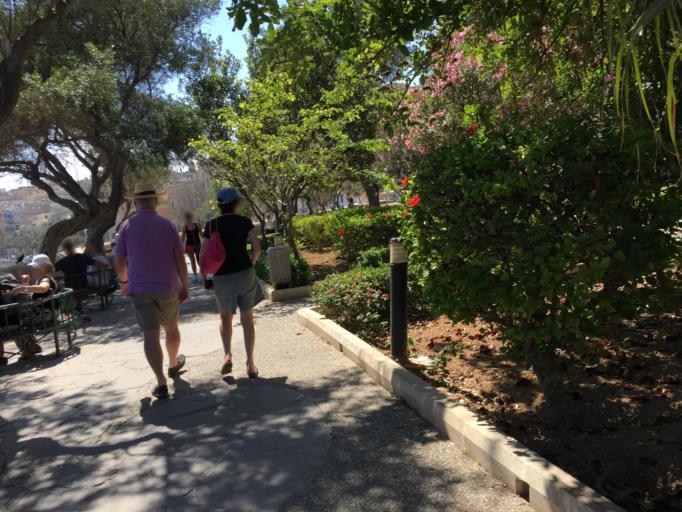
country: MT
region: Il-Belt Valletta
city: Valletta
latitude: 35.8973
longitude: 14.5175
